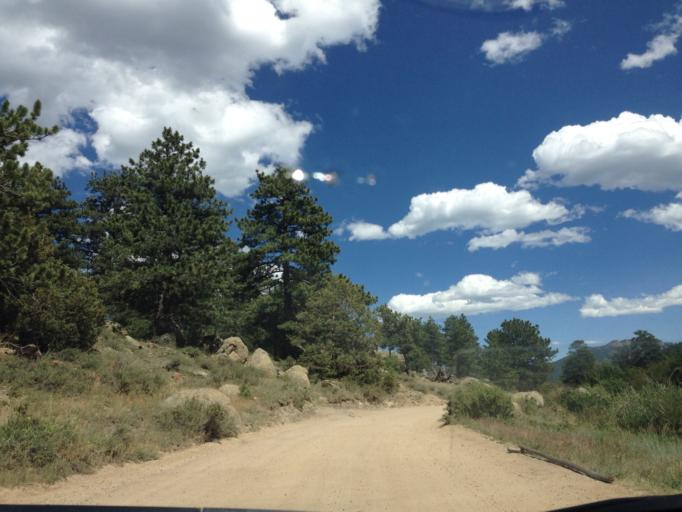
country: US
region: Colorado
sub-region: Larimer County
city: Estes Park
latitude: 40.3566
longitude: -105.6179
